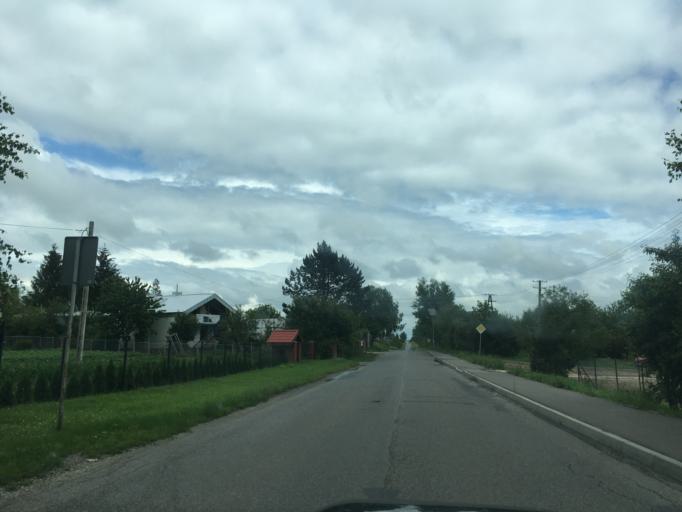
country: PL
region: Lublin Voivodeship
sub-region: Powiat swidnicki
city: Swidnik
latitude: 51.1946
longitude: 22.7119
